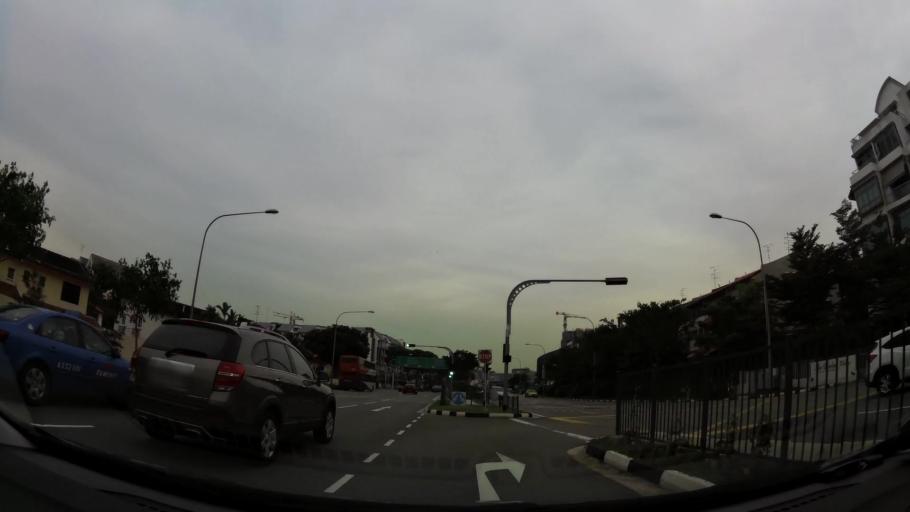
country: SG
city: Singapore
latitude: 1.3464
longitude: 103.8810
